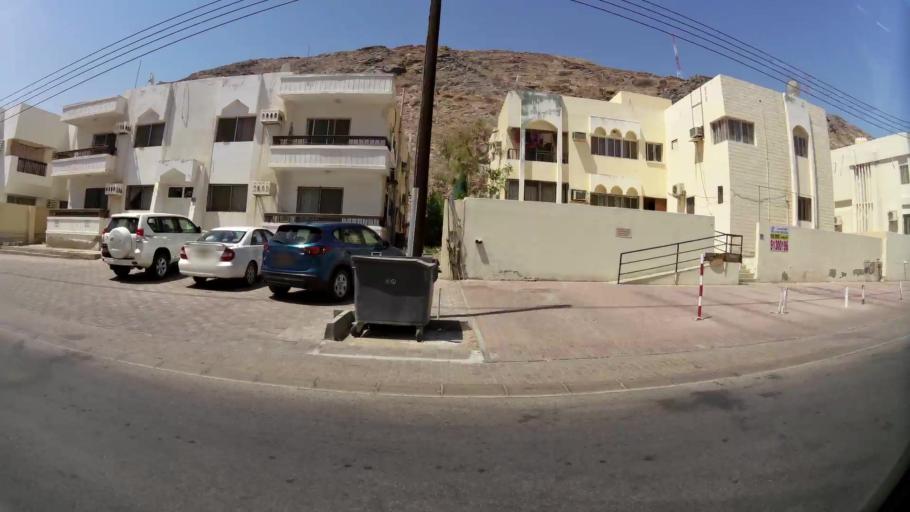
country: OM
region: Muhafazat Masqat
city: Muscat
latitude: 23.5956
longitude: 58.5398
